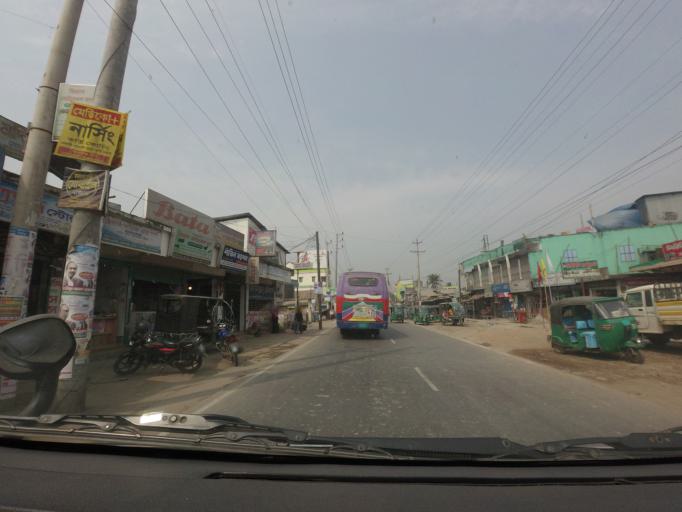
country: BD
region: Dhaka
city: Kishorganj
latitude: 24.3466
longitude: 90.7553
